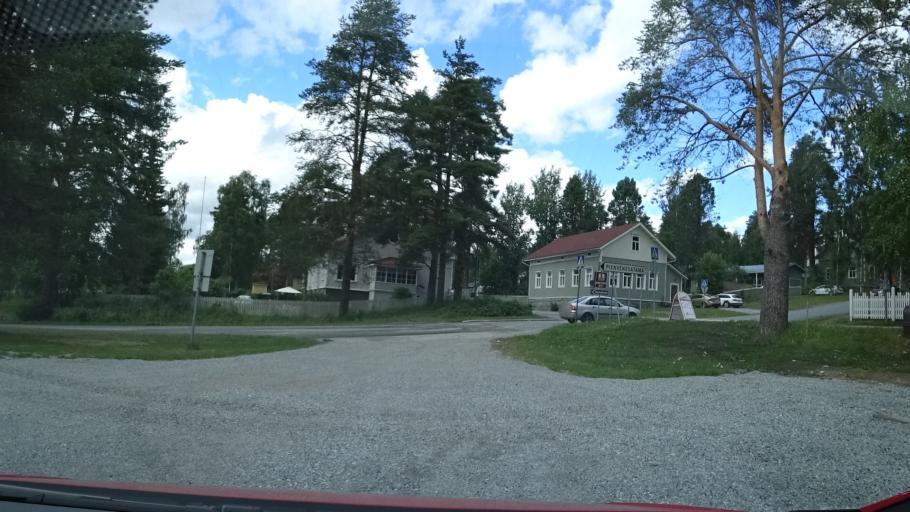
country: FI
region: North Karelia
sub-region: Pielisen Karjala
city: Nurmes
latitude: 63.5443
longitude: 29.1313
